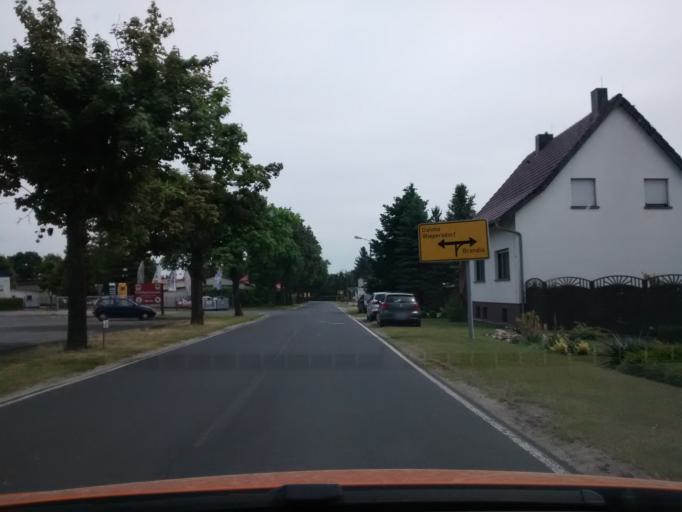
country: DE
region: Saxony-Anhalt
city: Holzdorf
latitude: 51.8159
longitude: 13.2167
